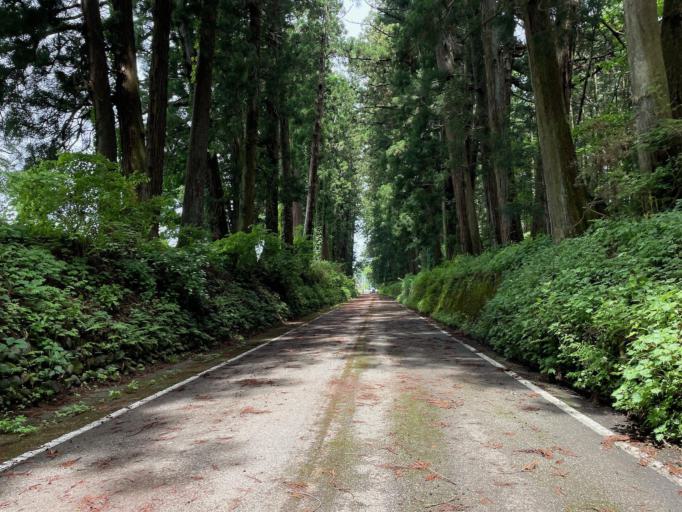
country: JP
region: Tochigi
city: Imaichi
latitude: 36.7046
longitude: 139.7488
